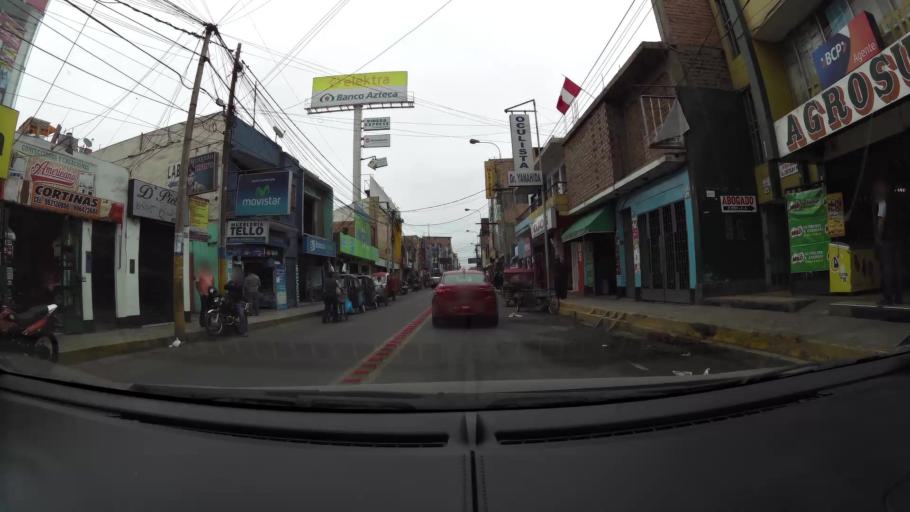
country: PE
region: Lima
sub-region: Barranca
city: Barranca
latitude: -10.7505
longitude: -77.7614
